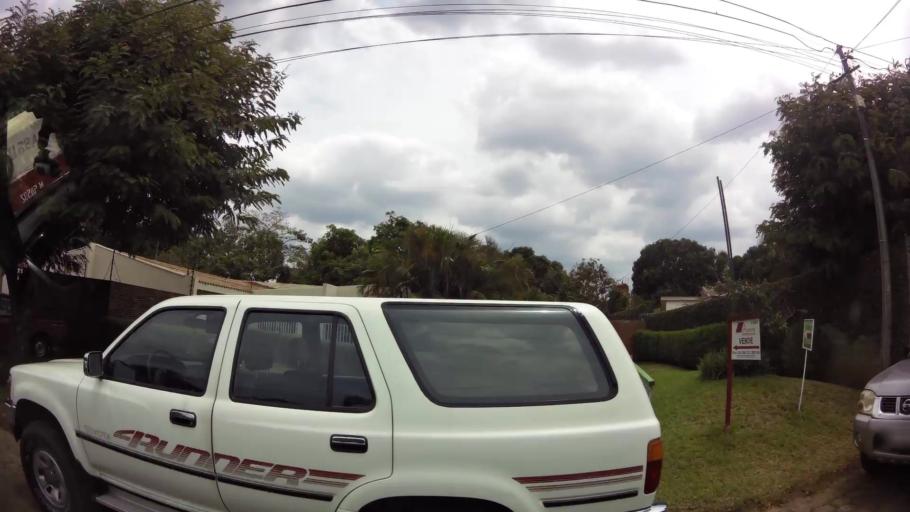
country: NI
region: Managua
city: Managua
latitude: 12.0912
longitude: -86.2276
